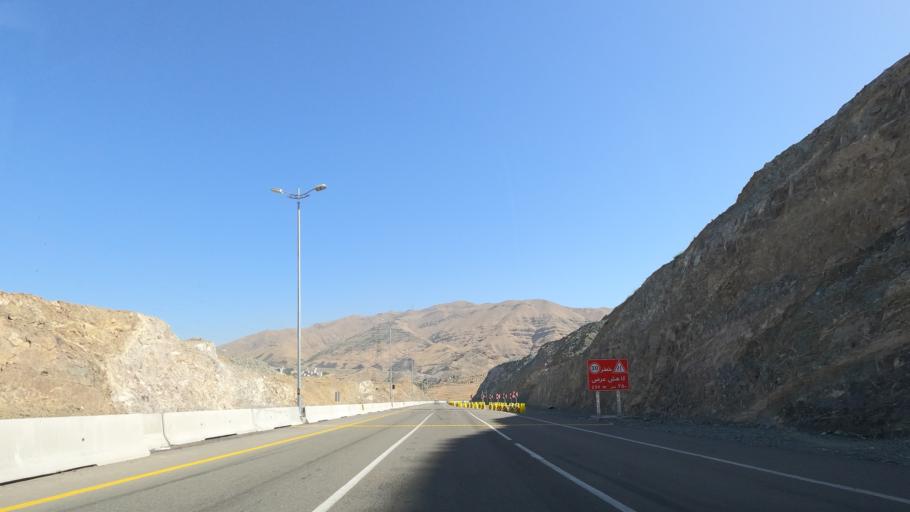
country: IR
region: Alborz
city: Karaj
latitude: 35.8190
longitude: 51.0378
